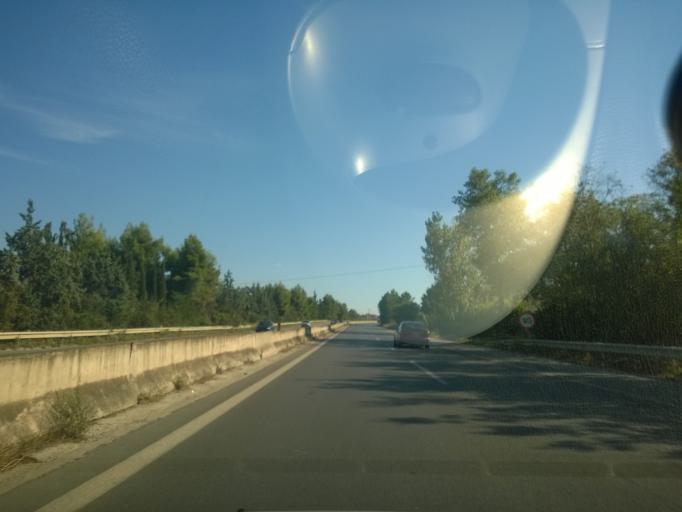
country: GR
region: Central Macedonia
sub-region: Nomos Thessalonikis
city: Kardia
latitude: 40.4690
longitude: 22.9956
